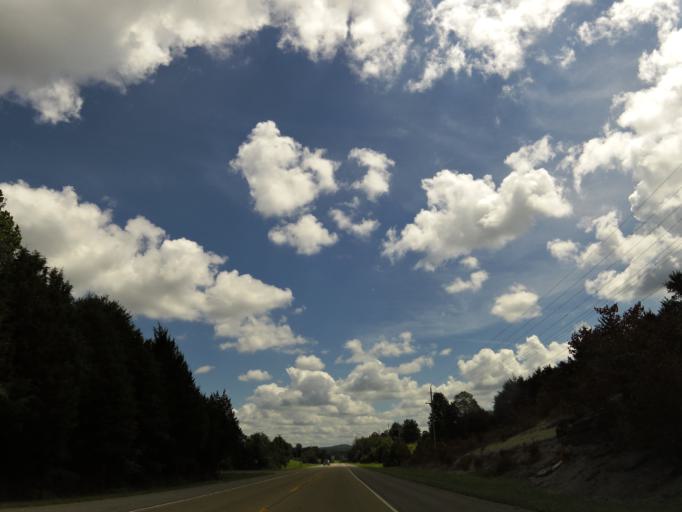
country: US
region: Kentucky
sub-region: Bell County
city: Middlesboro
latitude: 36.5288
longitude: -83.7315
